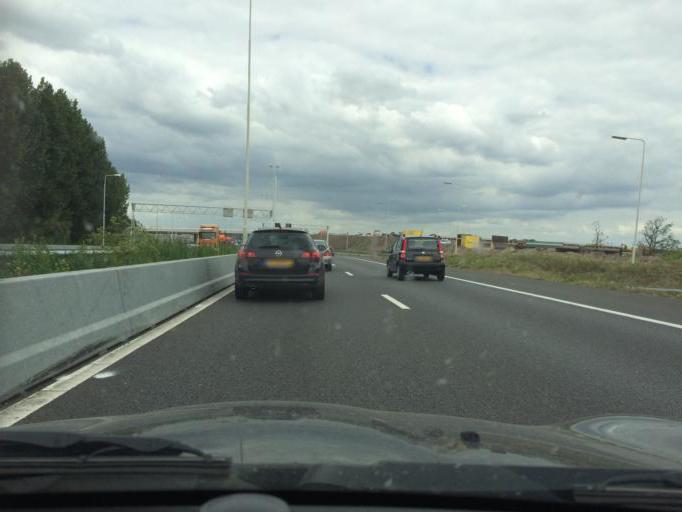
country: NL
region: South Holland
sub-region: Gemeente Waddinxveen
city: Waddinxveen
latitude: 52.0003
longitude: 4.6513
